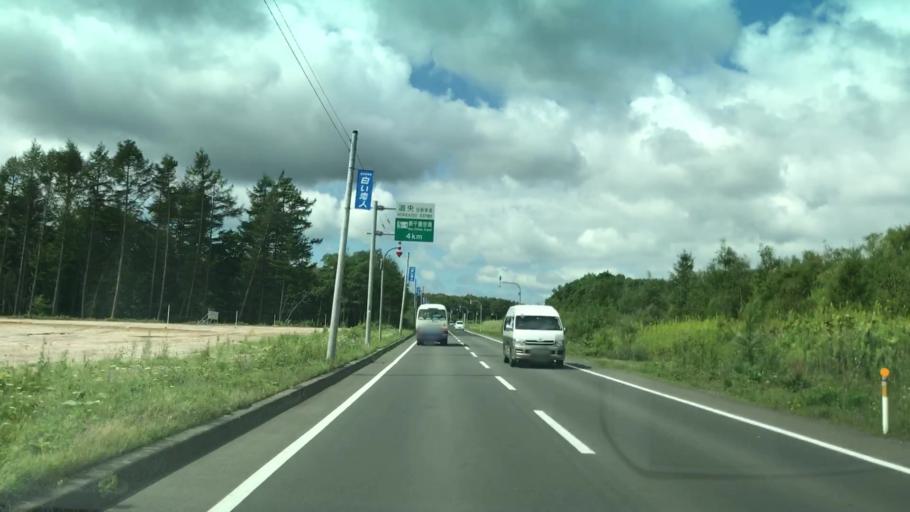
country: JP
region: Hokkaido
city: Chitose
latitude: 42.7632
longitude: 141.6722
